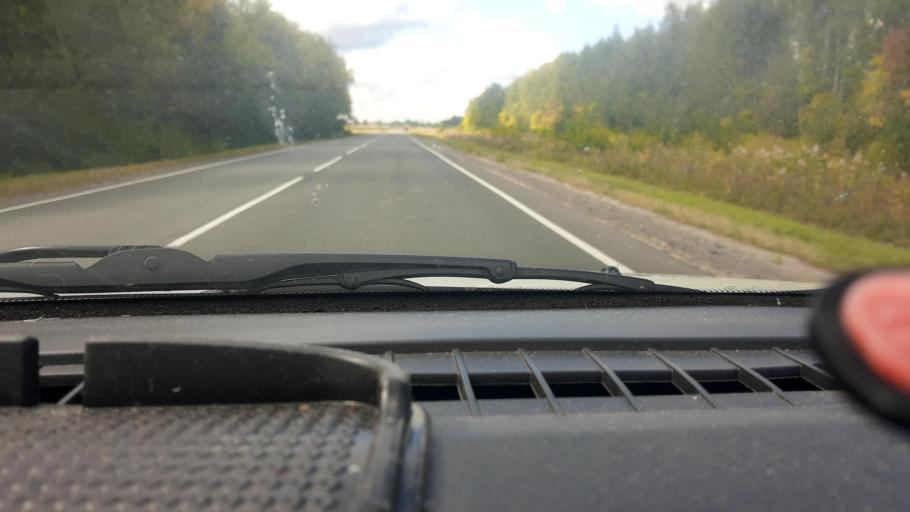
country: RU
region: Nizjnij Novgorod
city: Lukoyanov
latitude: 55.0622
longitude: 44.3577
